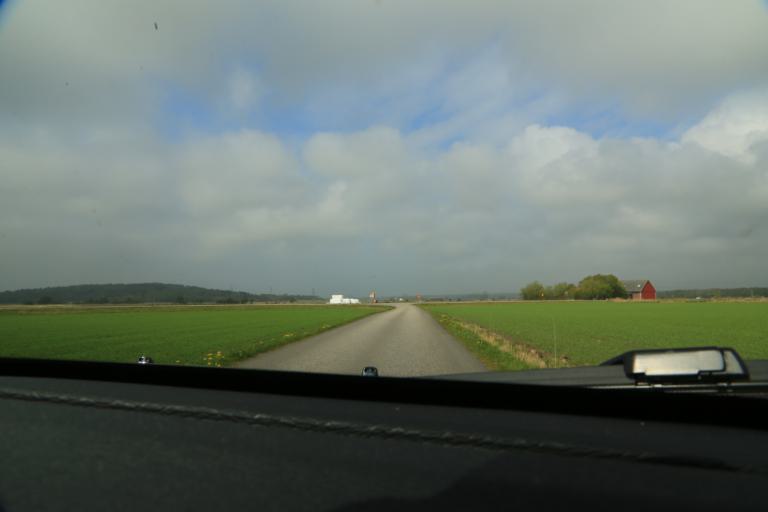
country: SE
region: Halland
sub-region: Kungsbacka Kommun
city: Frillesas
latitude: 57.2355
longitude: 12.1589
